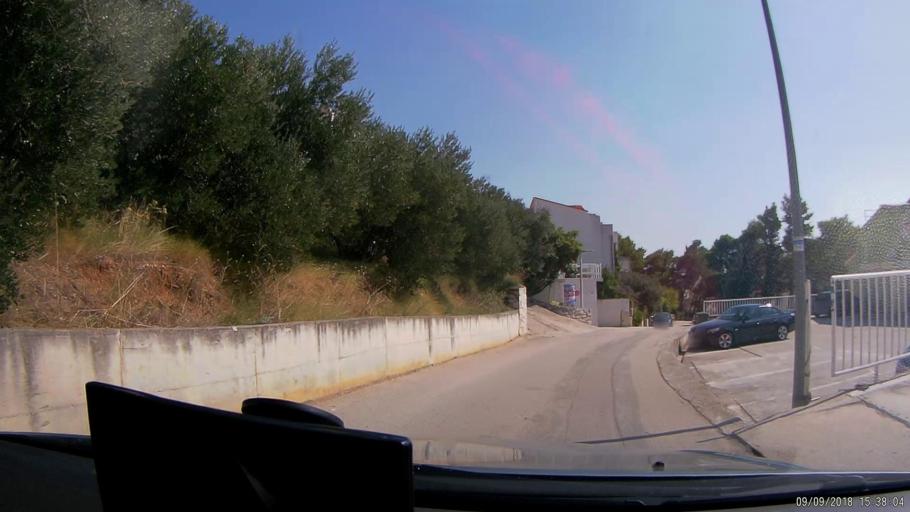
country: HR
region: Splitsko-Dalmatinska
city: Donja Brela
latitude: 43.3716
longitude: 16.9306
